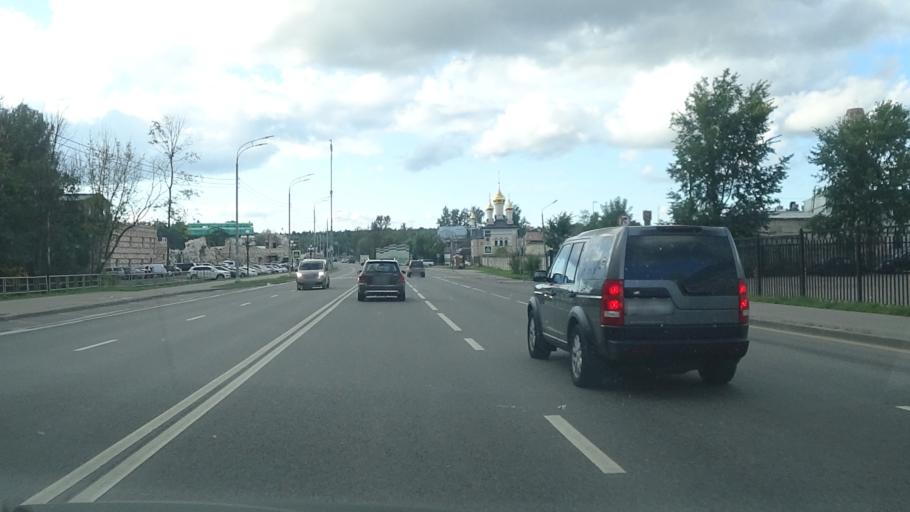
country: RU
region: Moskovskaya
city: Moskovskiy
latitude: 55.6154
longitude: 37.3459
